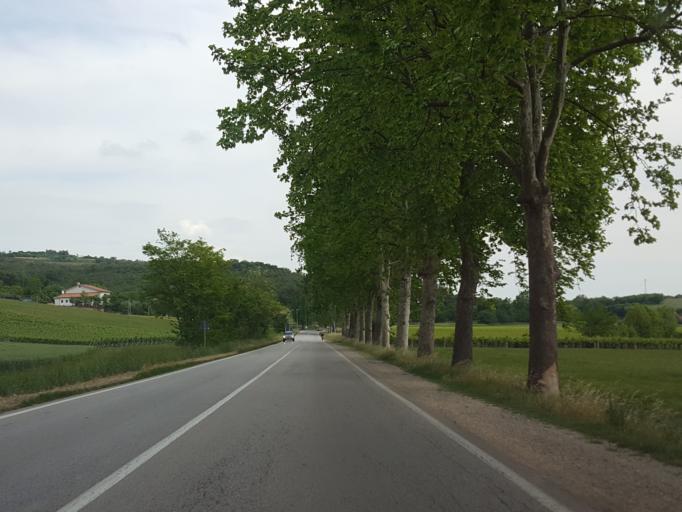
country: IT
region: Veneto
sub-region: Provincia di Vicenza
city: Alonte
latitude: 45.3568
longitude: 11.4379
